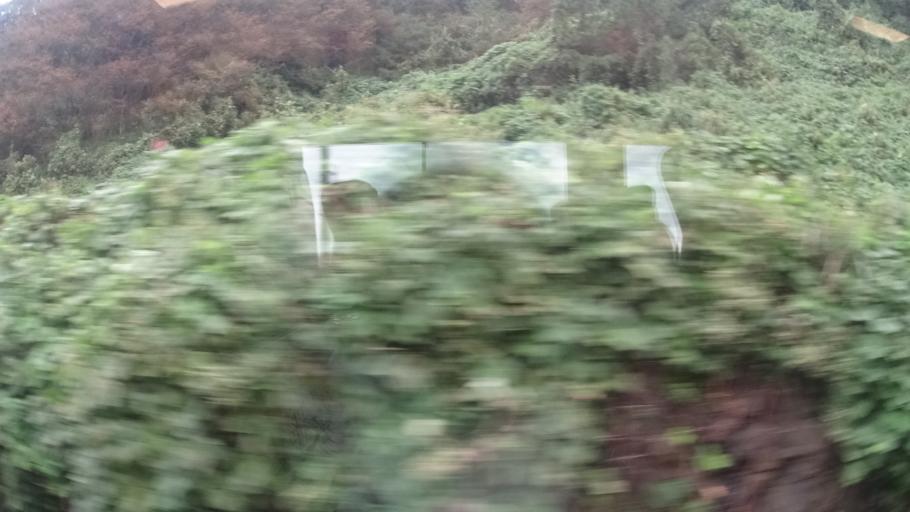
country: JP
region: Yamagata
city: Tsuruoka
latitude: 38.5486
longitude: 139.5505
